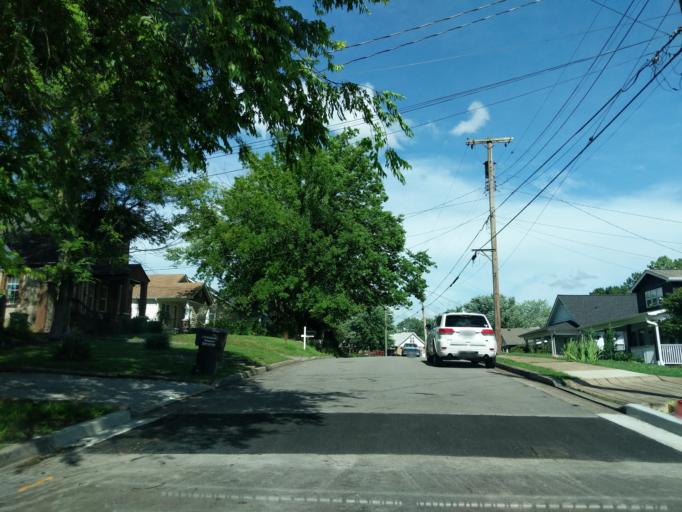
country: US
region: Tennessee
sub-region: Davidson County
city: Lakewood
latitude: 36.2690
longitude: -86.6656
